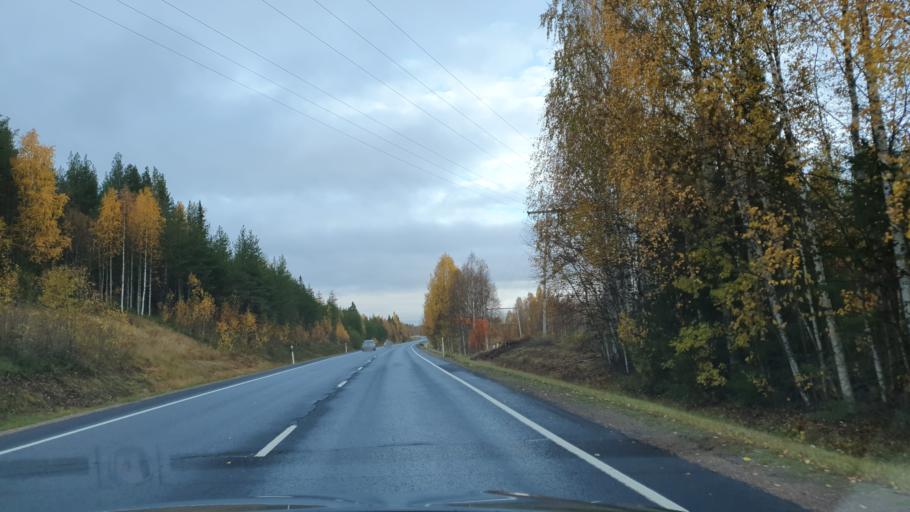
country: FI
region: Lapland
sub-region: Rovaniemi
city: Rovaniemi
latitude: 66.6052
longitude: 25.5779
